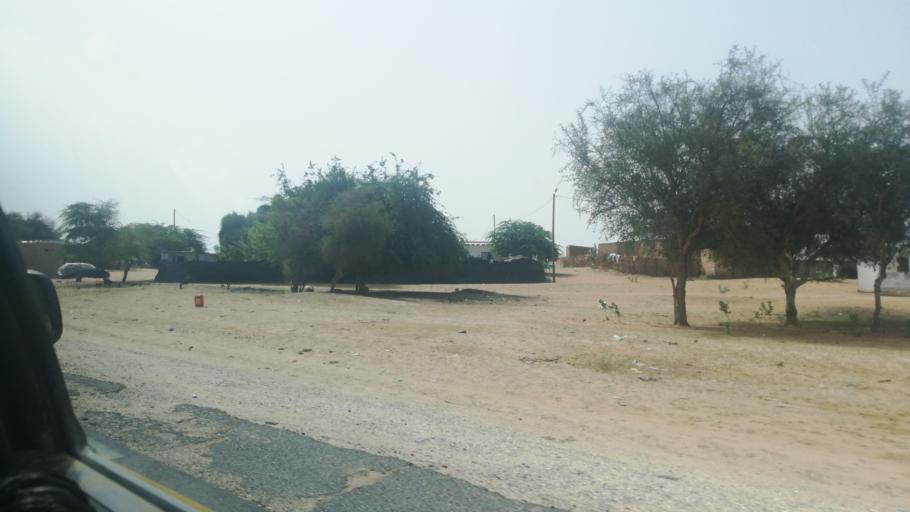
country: SN
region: Saint-Louis
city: Saint-Louis
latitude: 16.0750
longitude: -16.3836
